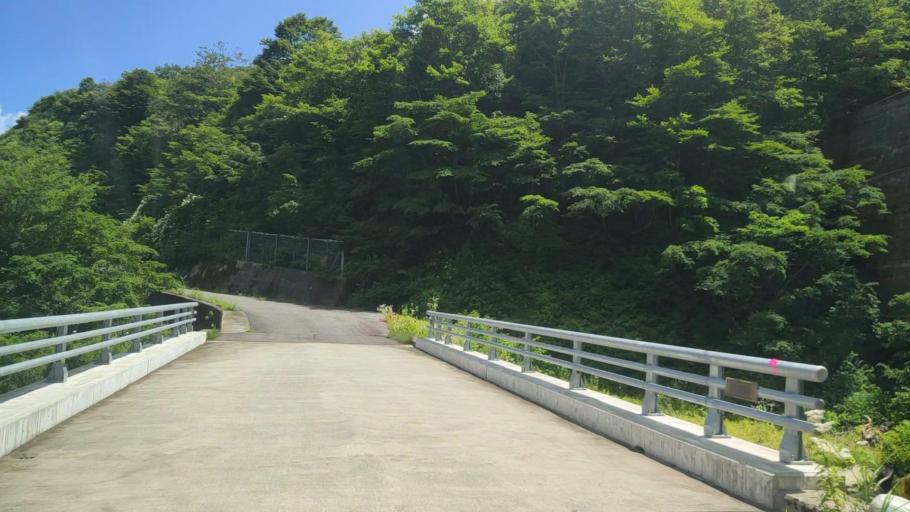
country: JP
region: Fukui
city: Ono
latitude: 35.7814
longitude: 136.5137
